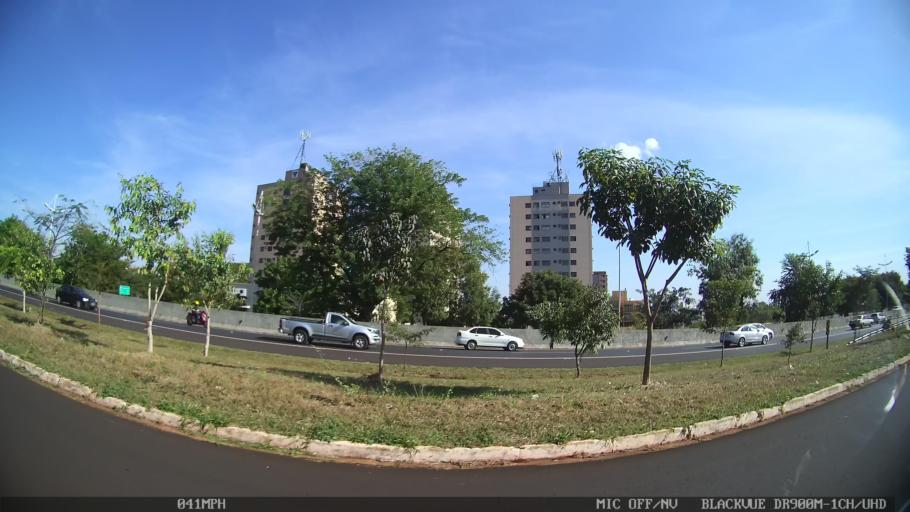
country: BR
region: Sao Paulo
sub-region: Ribeirao Preto
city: Ribeirao Preto
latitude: -21.1895
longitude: -47.7814
